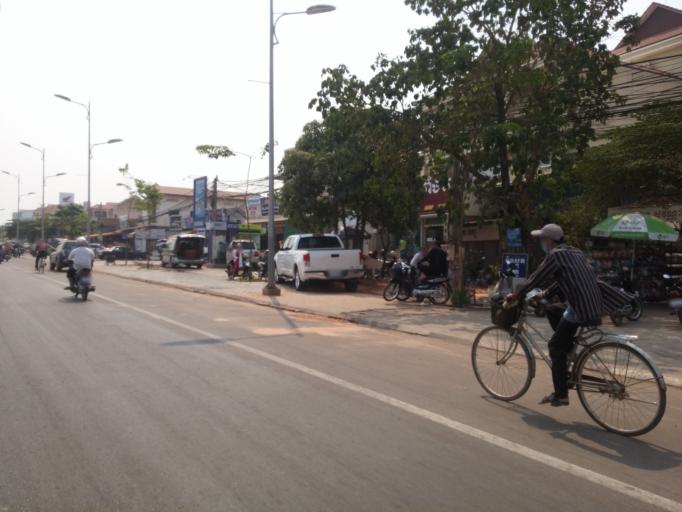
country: KH
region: Siem Reap
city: Siem Reap
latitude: 13.3605
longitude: 103.8633
